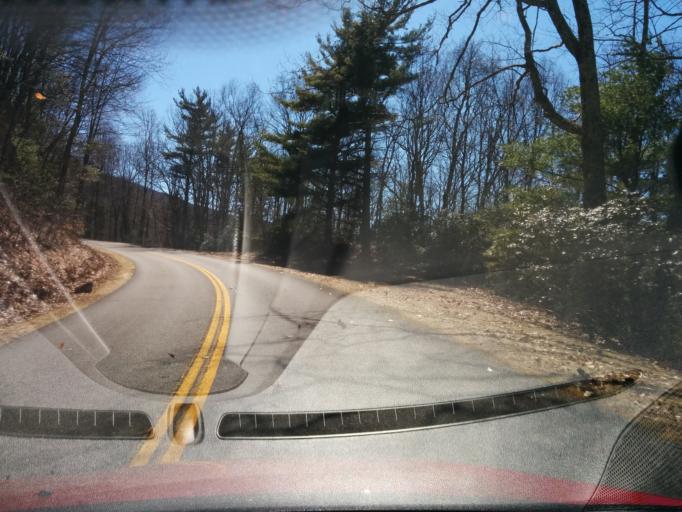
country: US
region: Virginia
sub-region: Augusta County
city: Stuarts Draft
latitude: 37.8485
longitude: -79.1559
